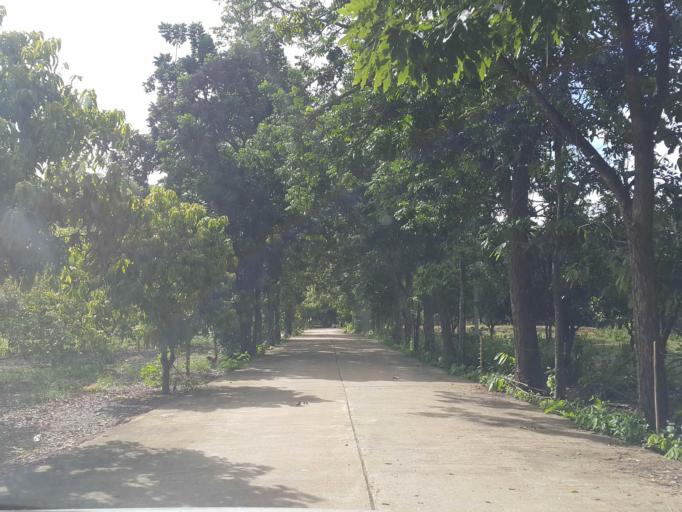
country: TH
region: Sukhothai
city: Thung Saliam
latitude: 17.2266
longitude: 99.5300
